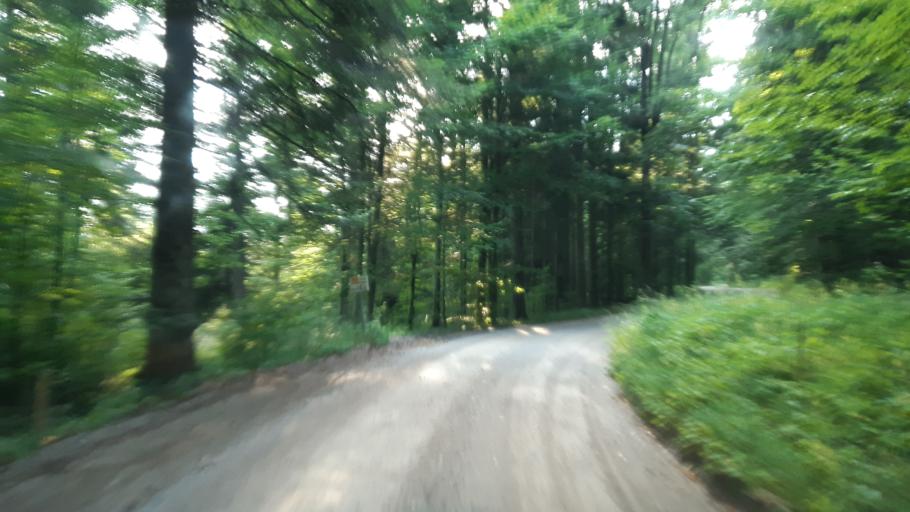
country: SI
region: Dolenjske Toplice
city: Dolenjske Toplice
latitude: 45.6723
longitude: 14.9956
